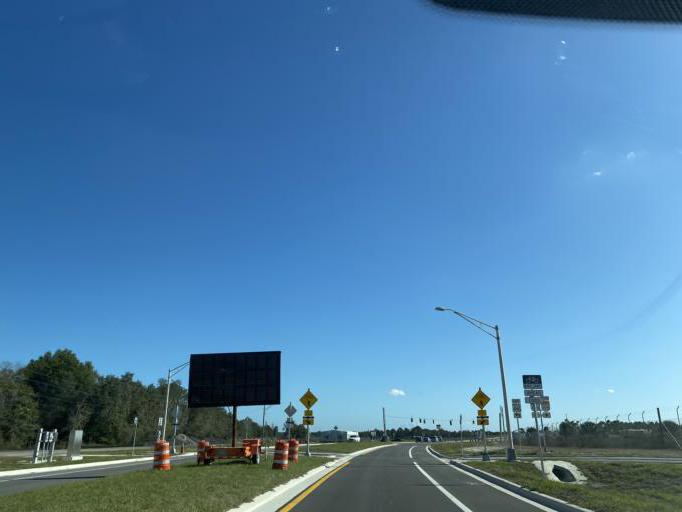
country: US
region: Florida
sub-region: Lake County
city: Mount Plymouth
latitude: 28.8125
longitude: -81.5132
